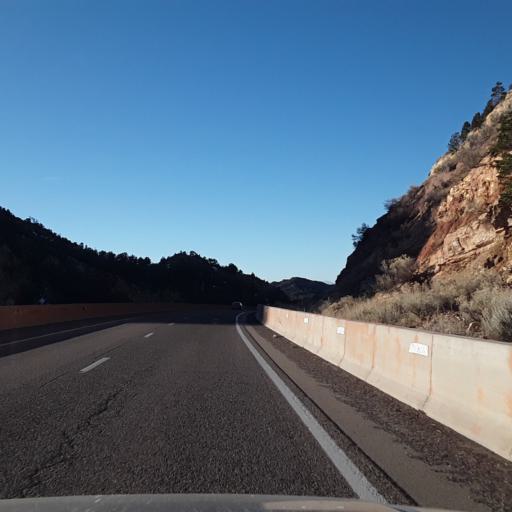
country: US
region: New Mexico
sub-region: Santa Fe County
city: Eldorado at Santa Fe
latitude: 35.5540
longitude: -105.8203
